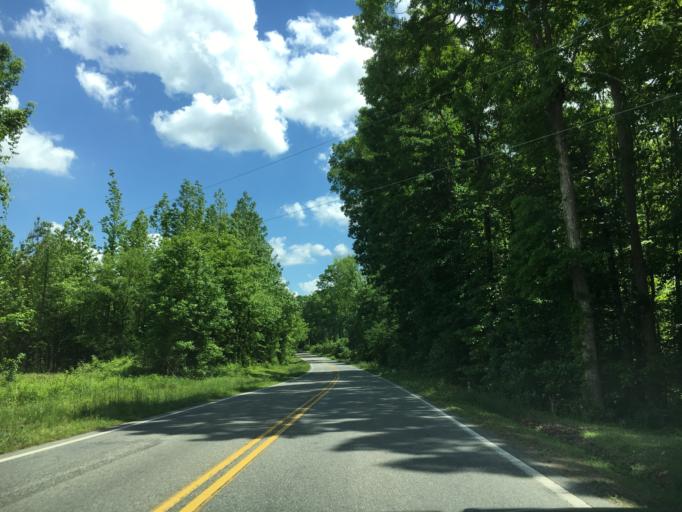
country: US
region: Virginia
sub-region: Halifax County
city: South Boston
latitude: 36.7163
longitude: -78.9396
